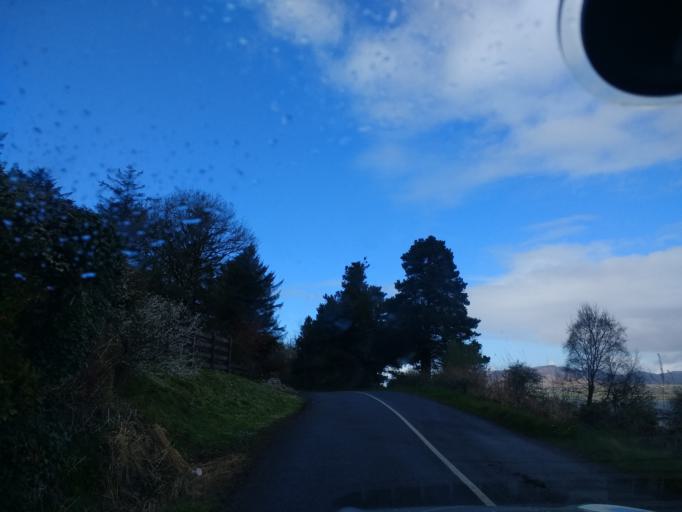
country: IE
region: Ulster
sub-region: County Donegal
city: Buncrana
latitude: 55.1484
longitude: -7.5474
